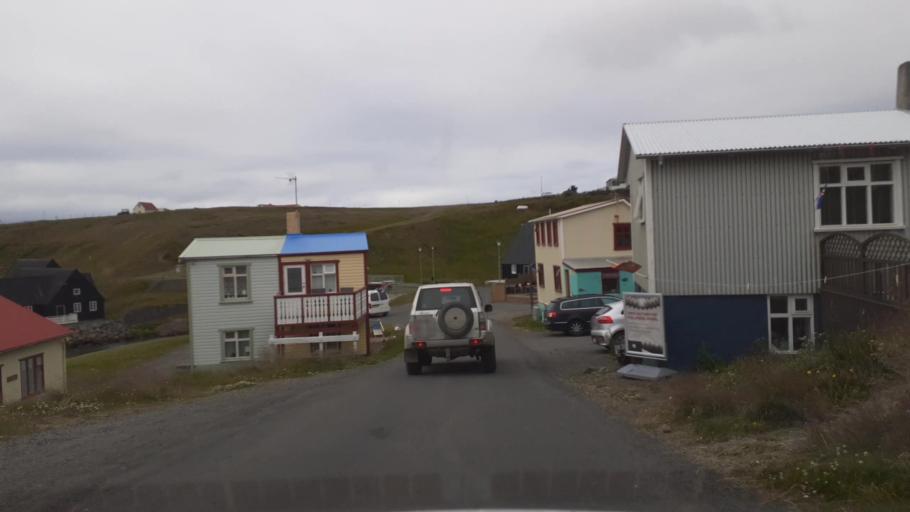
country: IS
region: Northwest
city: Saudarkrokur
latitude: 65.8983
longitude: -19.4161
